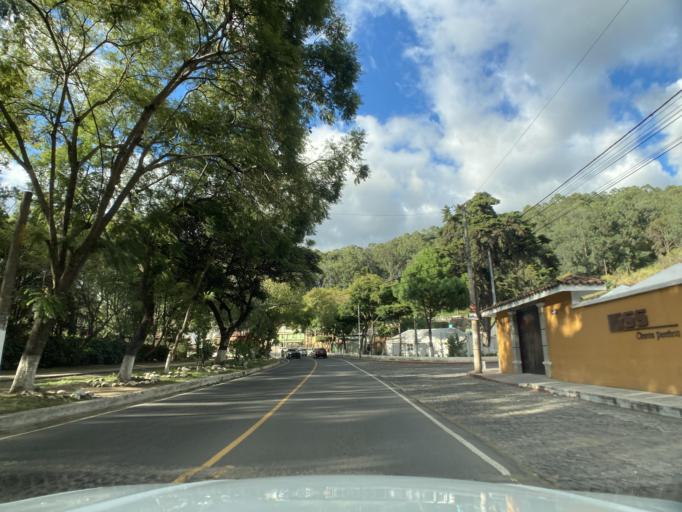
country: GT
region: Sacatepequez
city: Antigua Guatemala
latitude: 14.5648
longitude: -90.7353
